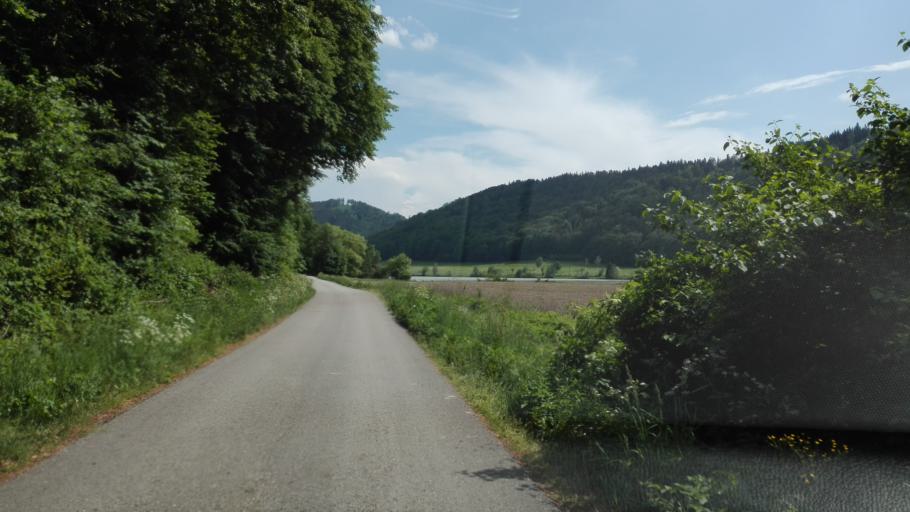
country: AT
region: Upper Austria
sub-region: Politischer Bezirk Rohrbach
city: Pfarrkirchen im Muehlkreis
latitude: 48.4404
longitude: 13.8606
